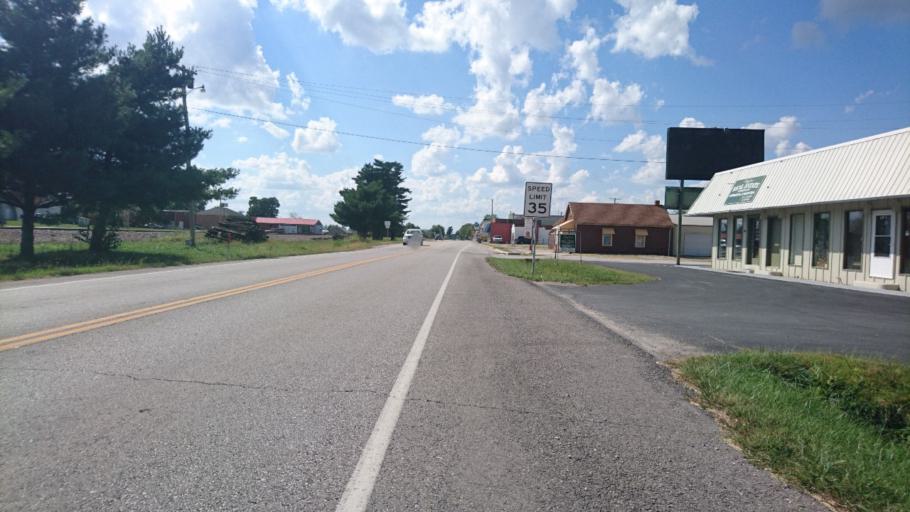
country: US
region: Missouri
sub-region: Greene County
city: Strafford
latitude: 37.2688
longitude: -93.1150
